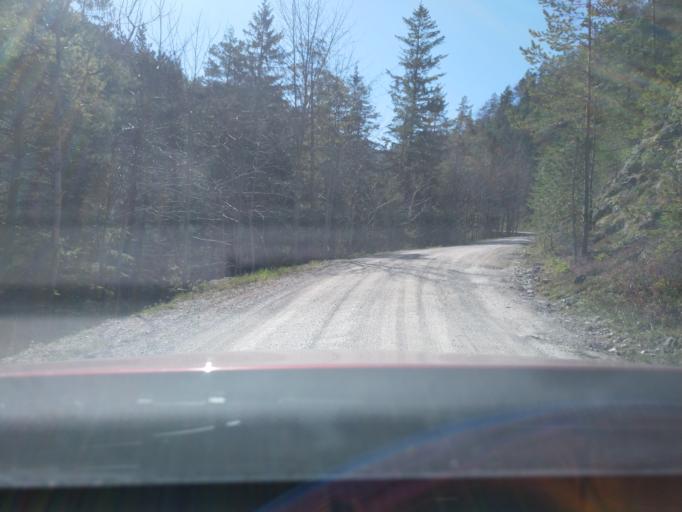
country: AT
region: Lower Austria
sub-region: Politischer Bezirk Wiener Neustadt
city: Gutenstein
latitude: 47.8210
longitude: 15.8444
